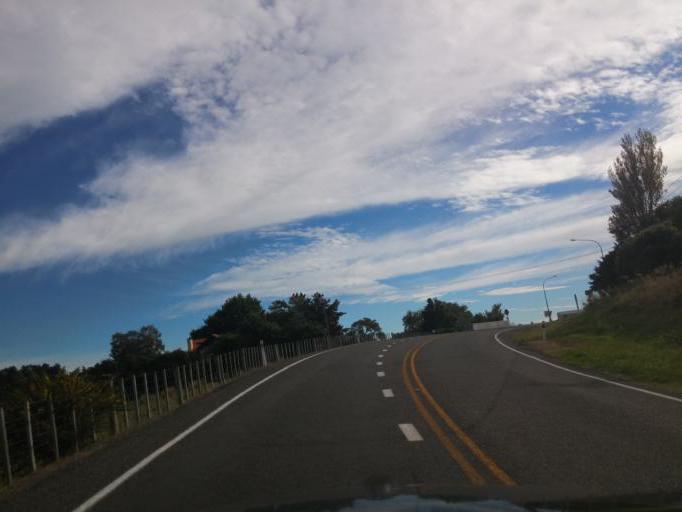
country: NZ
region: Manawatu-Wanganui
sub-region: Palmerston North City
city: Palmerston North
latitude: -40.3894
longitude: 175.6360
